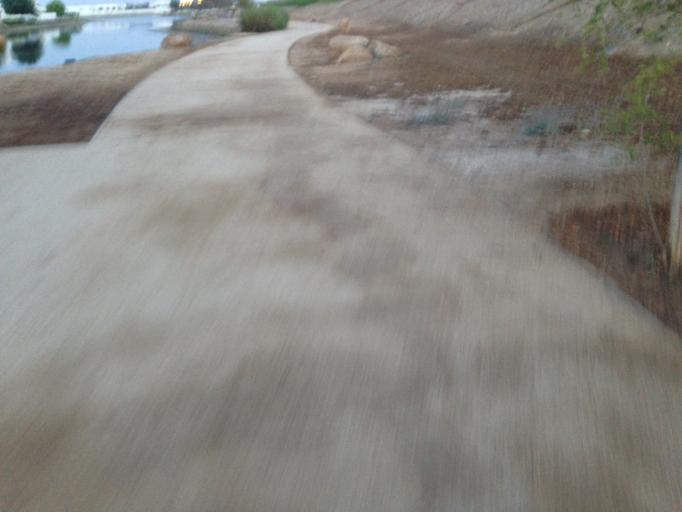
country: OM
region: Muhafazat Masqat
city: As Sib al Jadidah
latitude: 23.6227
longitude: 58.2691
